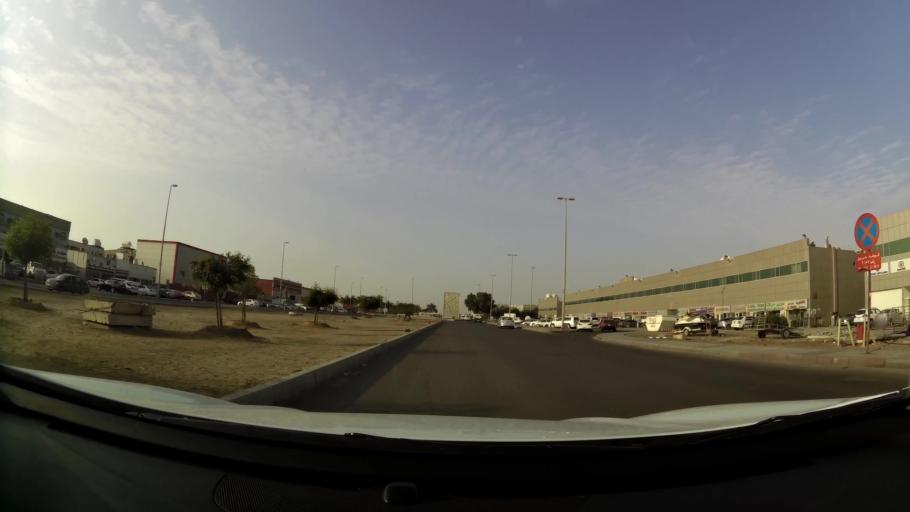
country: AE
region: Abu Dhabi
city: Abu Dhabi
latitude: 24.3713
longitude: 54.5162
